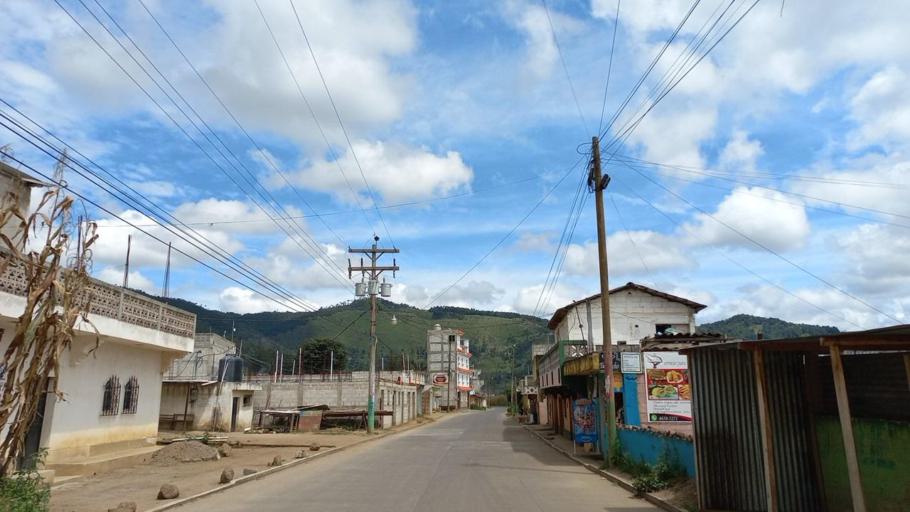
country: GT
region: Totonicapan
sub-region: Municipio de San Andres Xecul
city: San Andres Xecul
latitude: 14.8896
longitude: -91.4769
